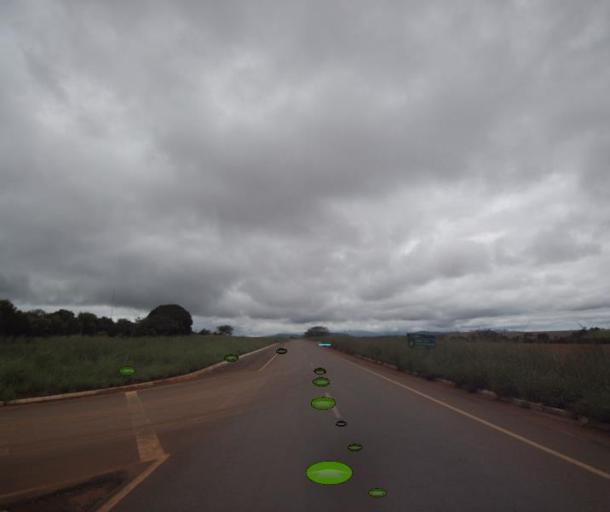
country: BR
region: Goias
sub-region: Barro Alto
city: Barro Alto
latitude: -14.8366
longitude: -49.0323
